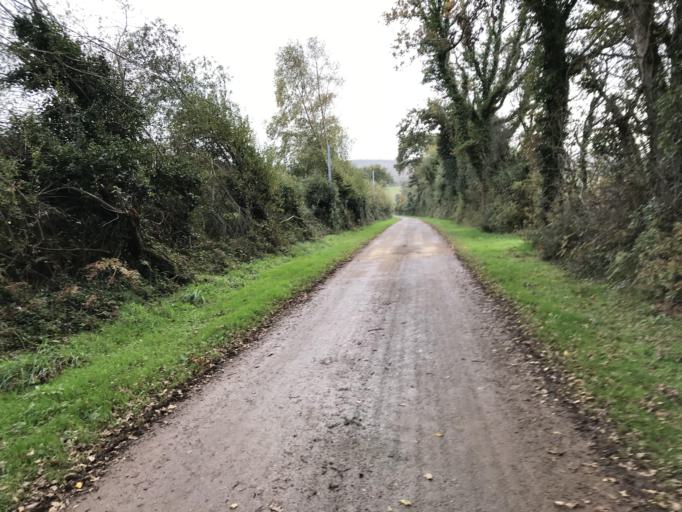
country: FR
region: Brittany
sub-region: Departement du Finistere
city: Irvillac
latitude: 48.3531
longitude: -4.2173
